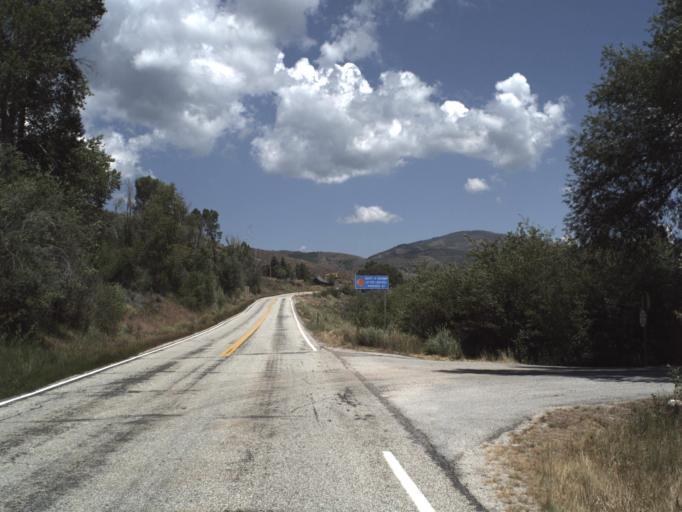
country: US
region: Utah
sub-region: Weber County
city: Wolf Creek
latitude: 41.2909
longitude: -111.6379
